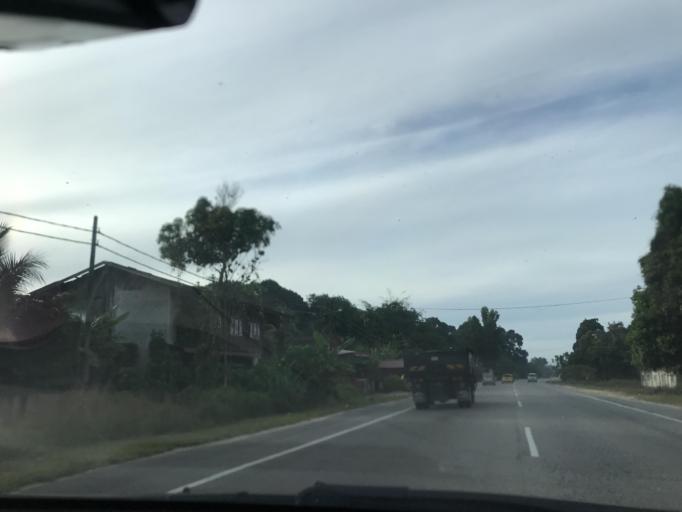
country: MY
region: Kelantan
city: Kampung Lemal
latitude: 6.0038
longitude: 102.1823
